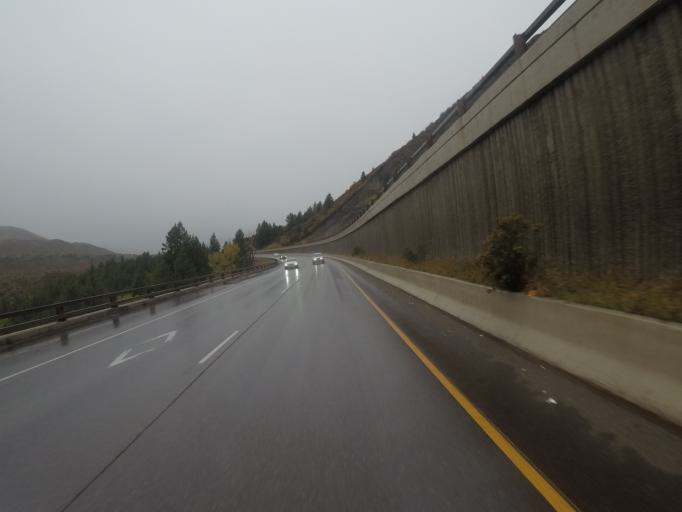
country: US
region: Colorado
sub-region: Pitkin County
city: Snowmass Village
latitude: 39.2443
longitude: -106.8814
